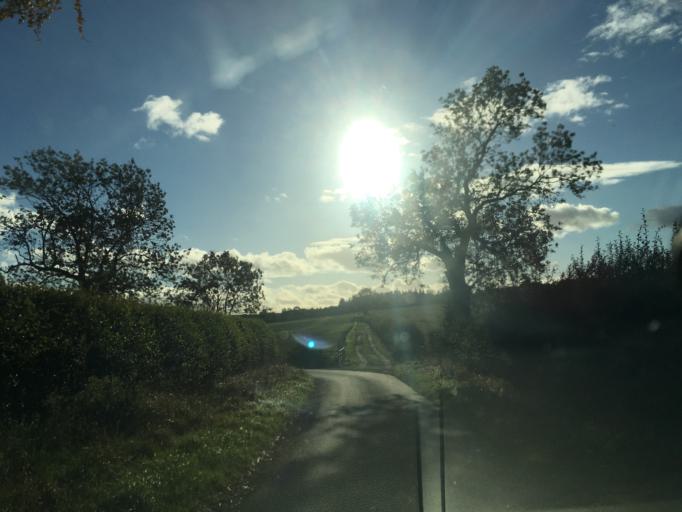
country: GB
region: Scotland
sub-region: East Lothian
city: Pencaitland
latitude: 55.8638
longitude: -2.9086
